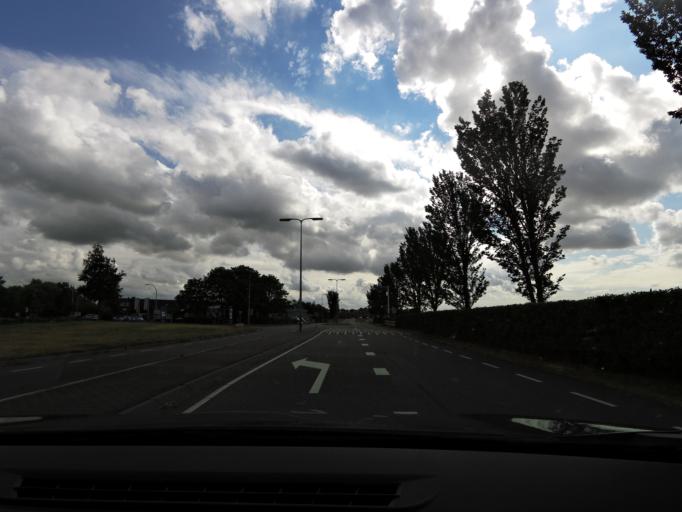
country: NL
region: South Holland
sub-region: Gemeente Delft
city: Delft
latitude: 51.9812
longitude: 4.3172
